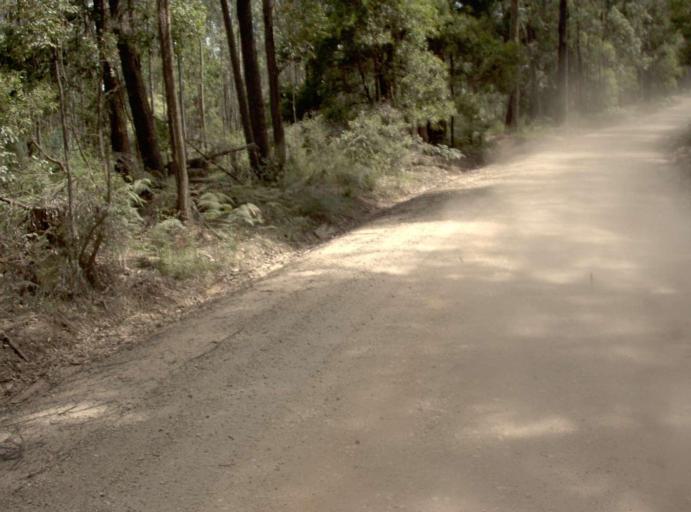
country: AU
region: Victoria
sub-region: East Gippsland
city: Lakes Entrance
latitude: -37.6316
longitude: 148.6759
